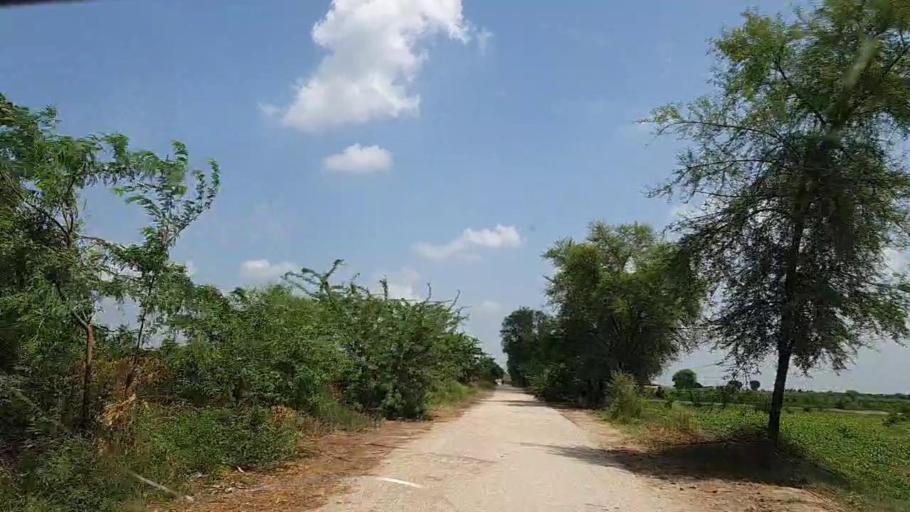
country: PK
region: Sindh
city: Tharu Shah
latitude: 26.9974
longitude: 68.0684
